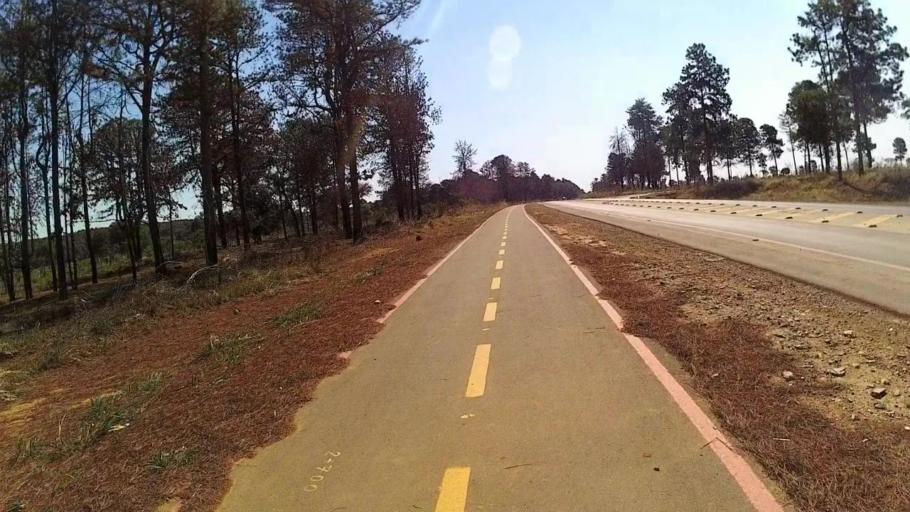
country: BR
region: Federal District
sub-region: Brasilia
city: Brasilia
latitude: -15.6775
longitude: -48.2053
